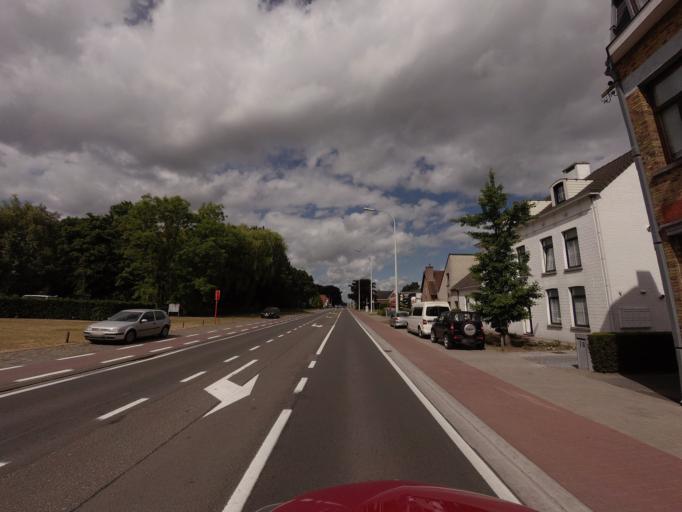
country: BE
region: Flanders
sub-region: Provincie Oost-Vlaanderen
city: Maldegem
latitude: 51.2047
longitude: 3.4861
